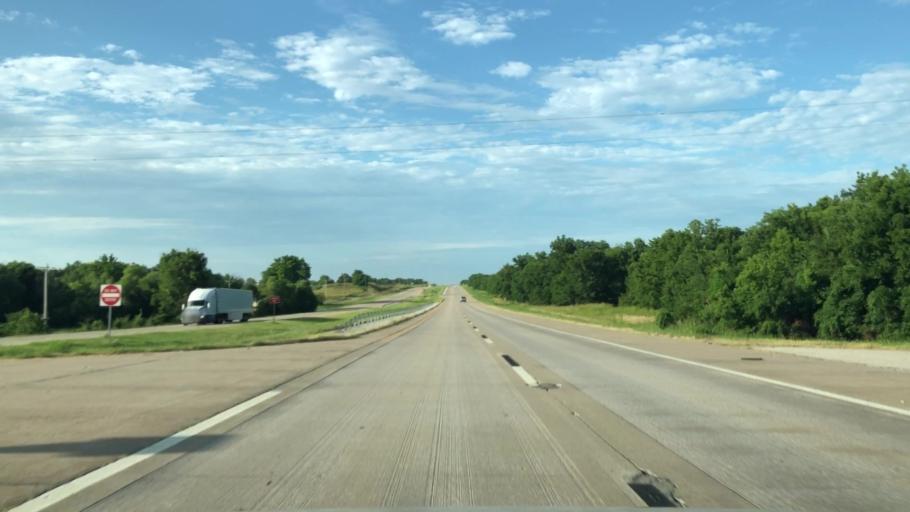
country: US
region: Oklahoma
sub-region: Osage County
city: Skiatook
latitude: 36.4420
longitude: -95.9206
